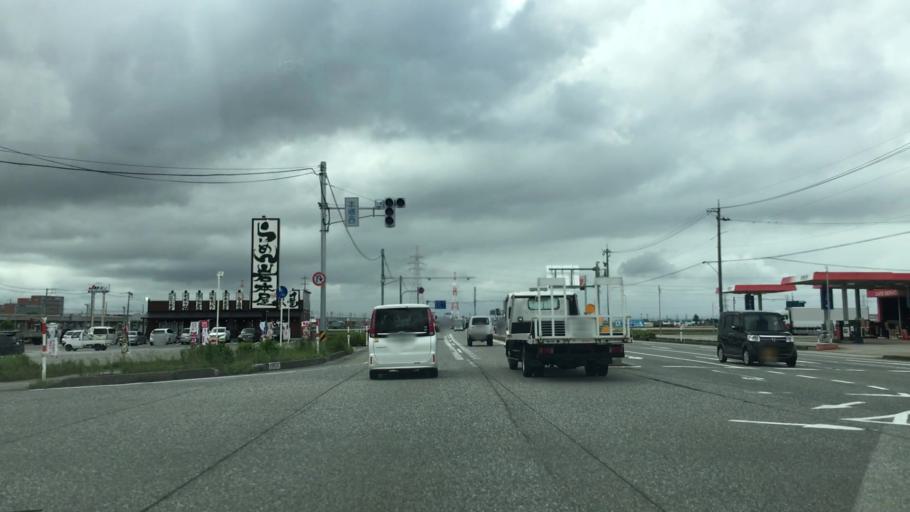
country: JP
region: Toyama
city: Kuragaki-kosugi
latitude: 36.7260
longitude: 137.1496
